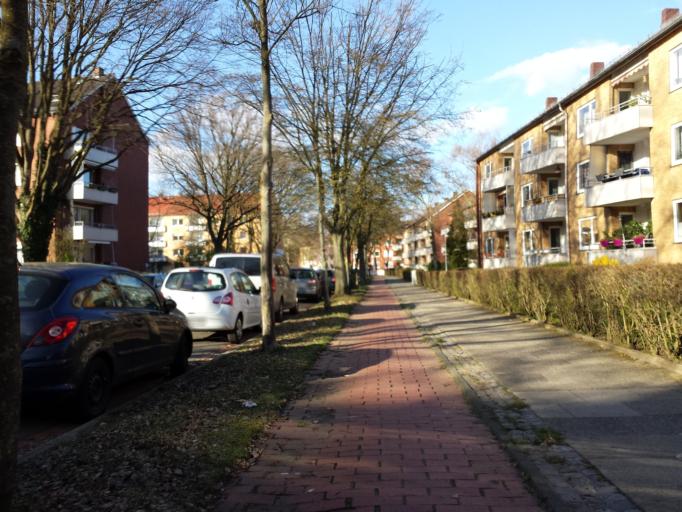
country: DE
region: Bremen
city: Bremen
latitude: 53.0906
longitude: 8.8539
